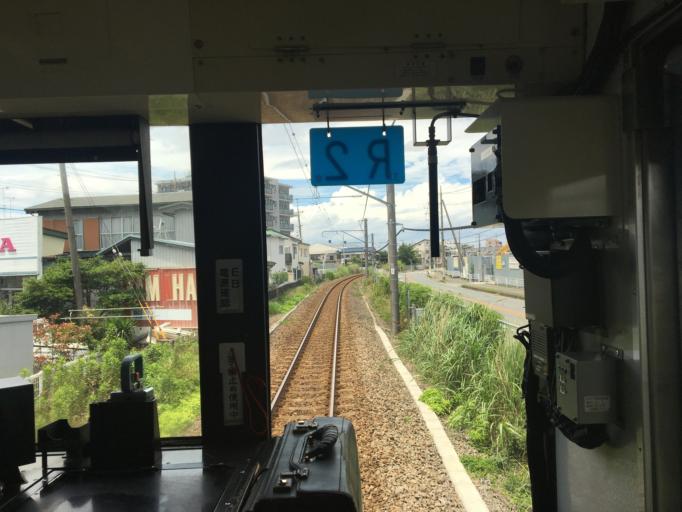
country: JP
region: Kanagawa
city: Atsugi
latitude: 35.4091
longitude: 139.3788
